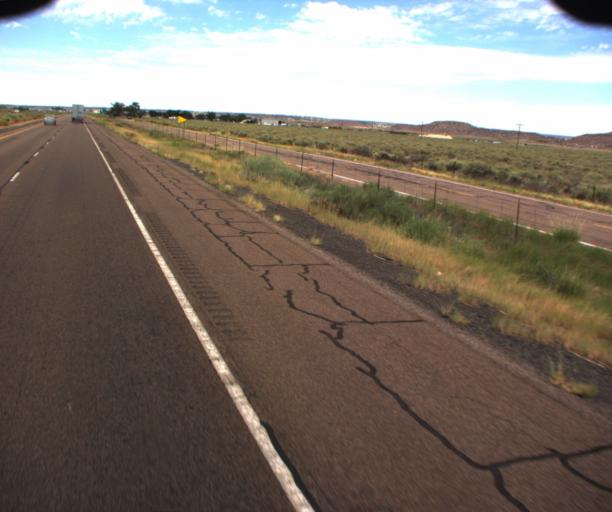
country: US
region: Arizona
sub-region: Apache County
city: Houck
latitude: 35.1992
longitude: -109.3952
